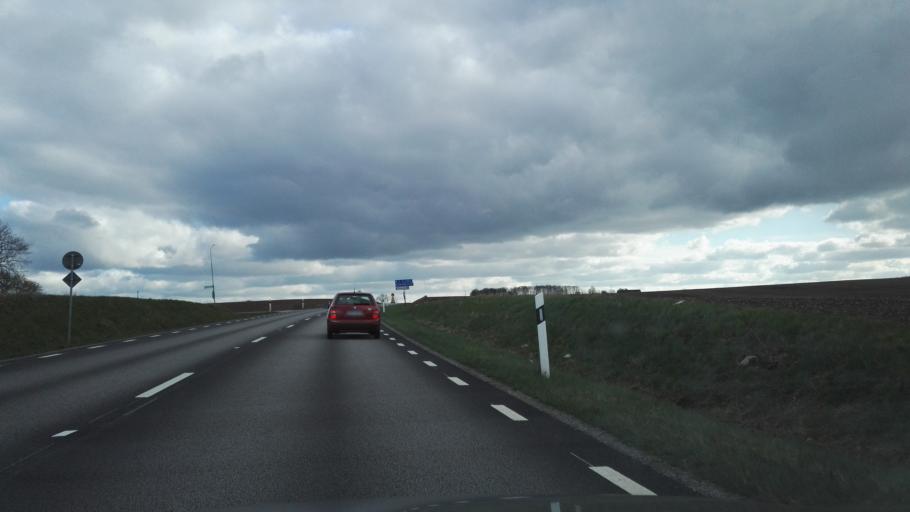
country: SE
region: Skane
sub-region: Sjobo Kommun
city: Sjoebo
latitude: 55.6824
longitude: 13.7171
